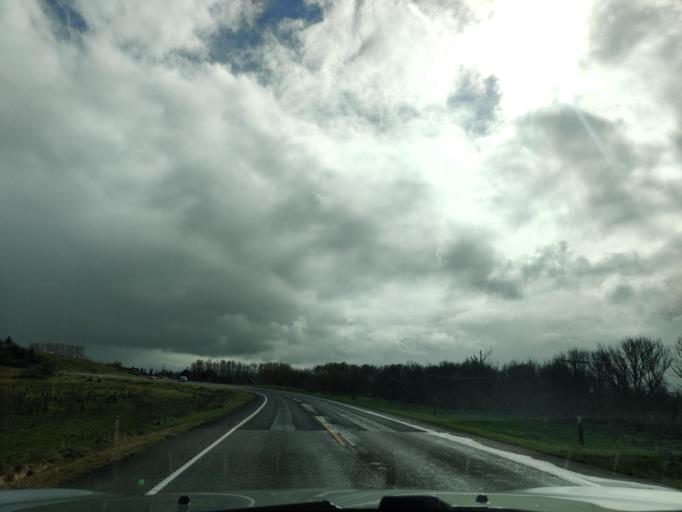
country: NZ
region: Hawke's Bay
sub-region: Hastings District
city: Hastings
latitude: -39.9750
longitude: 176.4958
